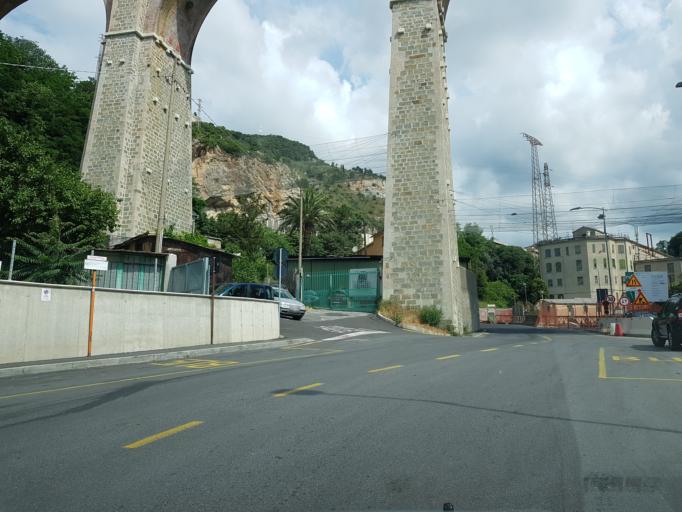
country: IT
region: Liguria
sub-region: Provincia di Genova
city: San Teodoro
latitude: 44.4351
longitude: 8.8546
